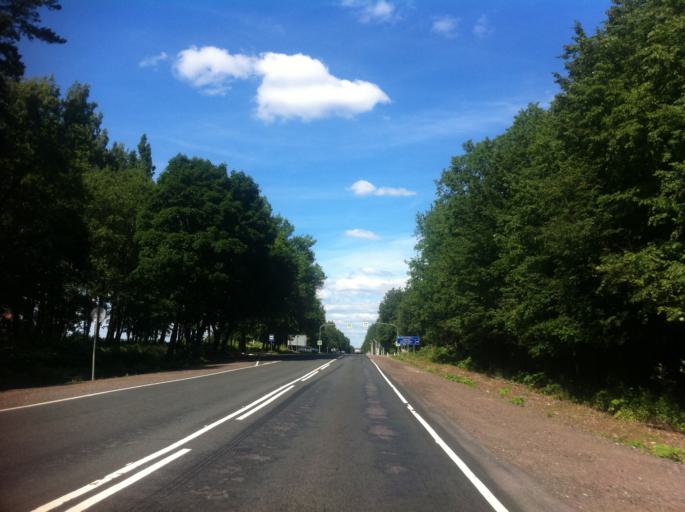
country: RU
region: Leningrad
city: Luga
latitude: 58.5844
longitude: 29.8215
